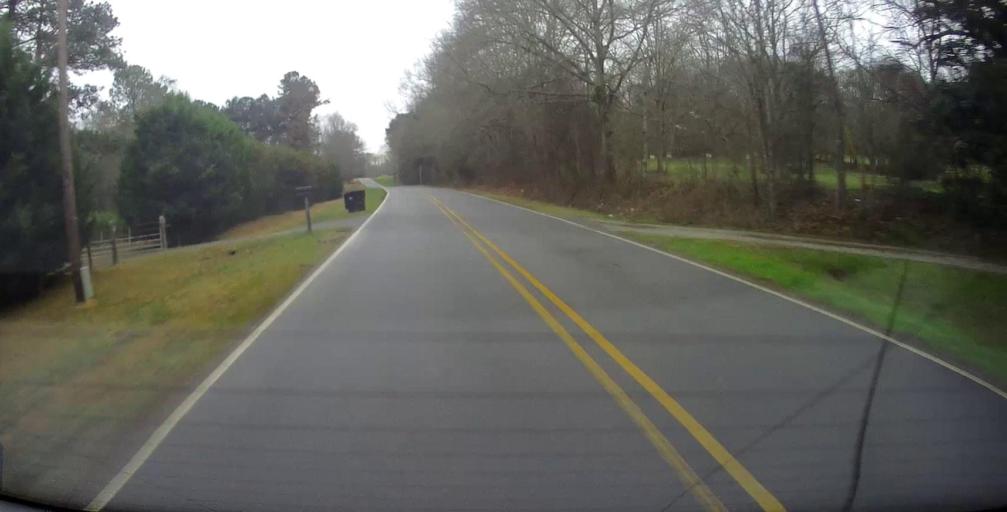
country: US
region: Georgia
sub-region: Pike County
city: Zebulon
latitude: 33.0684
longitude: -84.3273
